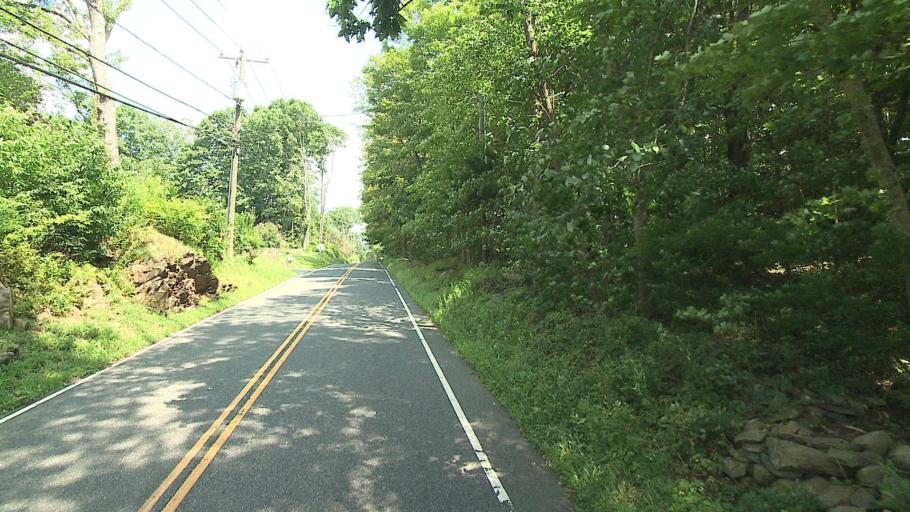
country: US
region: Connecticut
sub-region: Litchfield County
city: New Preston
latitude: 41.6543
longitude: -73.2849
